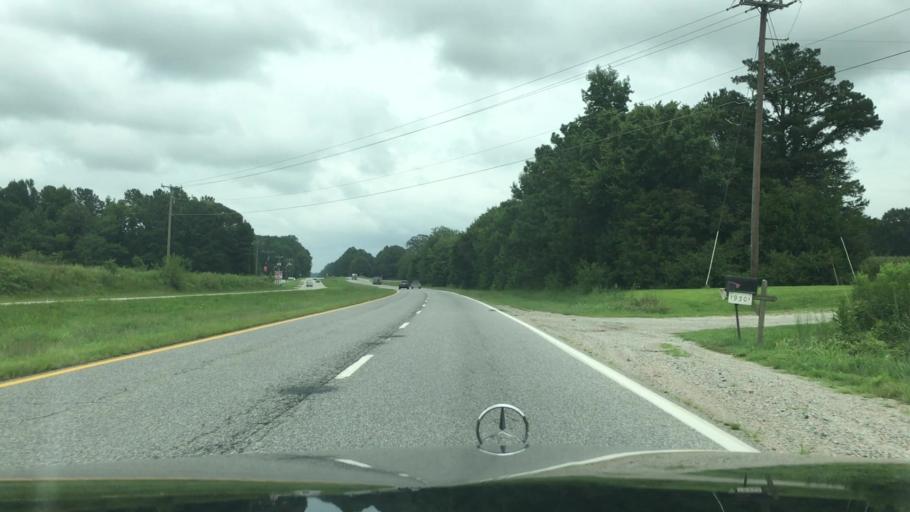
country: US
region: Virginia
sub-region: Amelia County
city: Amelia Court House
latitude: 37.3193
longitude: -78.0422
